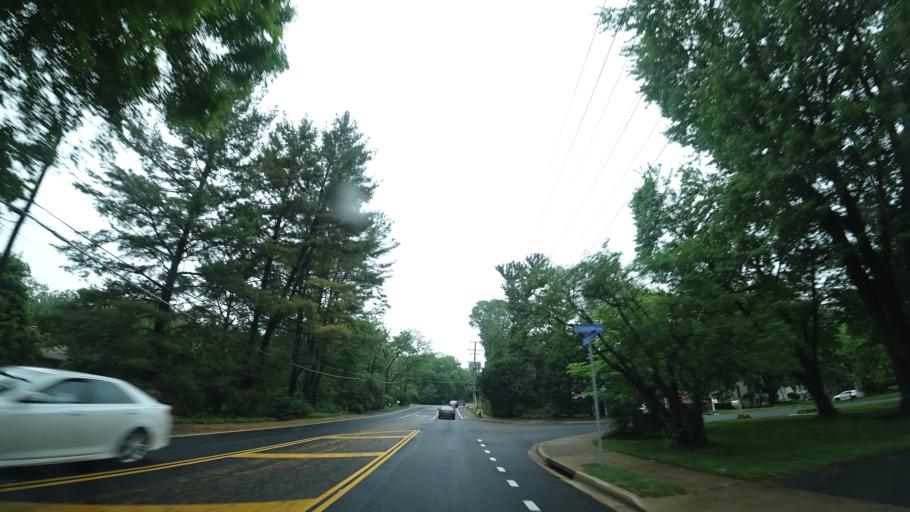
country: US
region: Virginia
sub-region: Fairfax County
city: Tysons Corner
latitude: 38.9403
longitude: -77.2144
